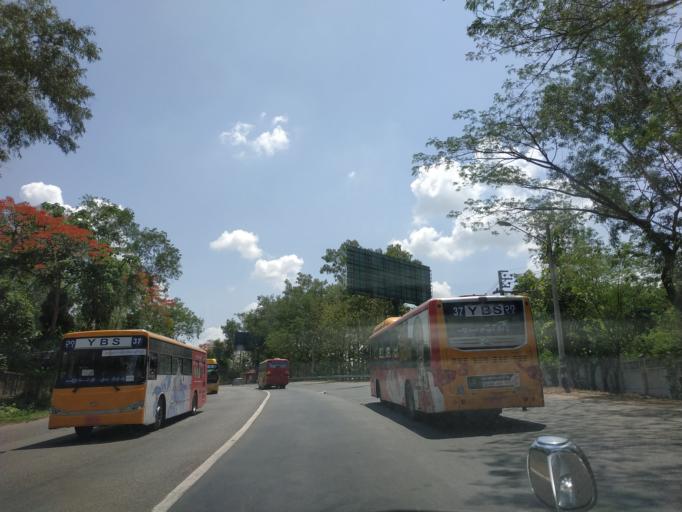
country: MM
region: Yangon
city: Yangon
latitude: 16.9903
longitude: 96.1302
